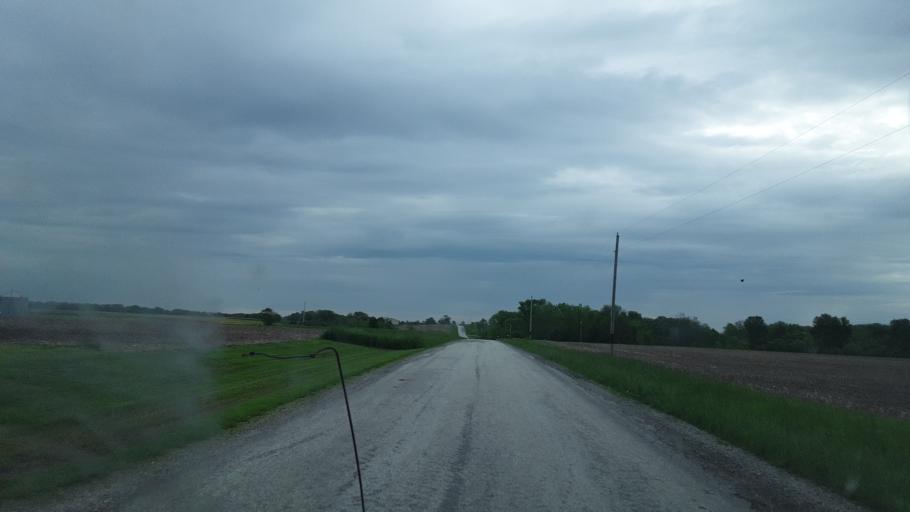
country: US
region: Illinois
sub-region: McDonough County
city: Macomb
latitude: 40.3816
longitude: -90.6122
